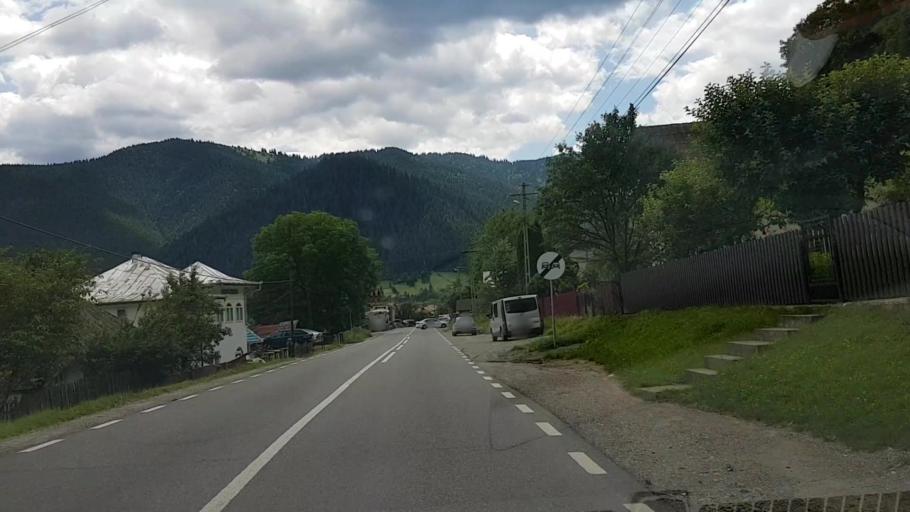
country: RO
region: Neamt
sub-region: Comuna Borca
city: Borca
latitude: 47.2113
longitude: 25.7556
